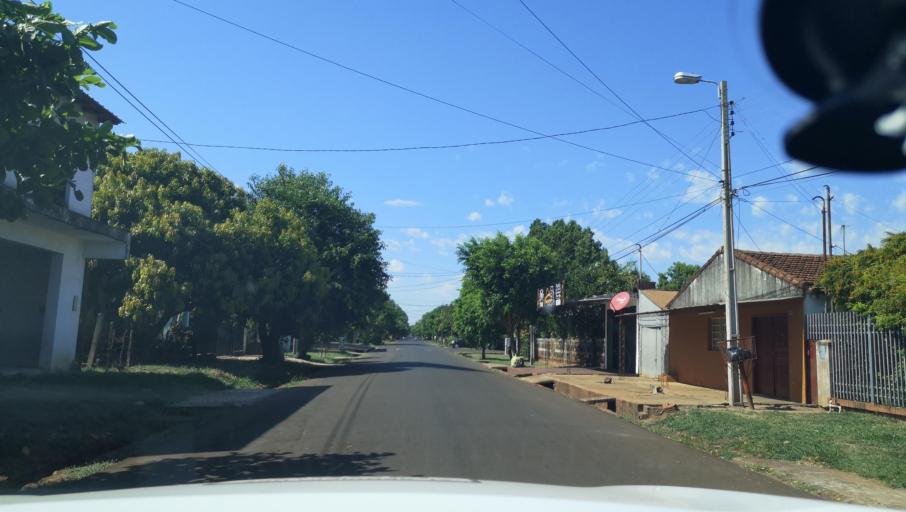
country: PY
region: Itapua
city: Carmen del Parana
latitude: -27.1645
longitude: -56.2338
